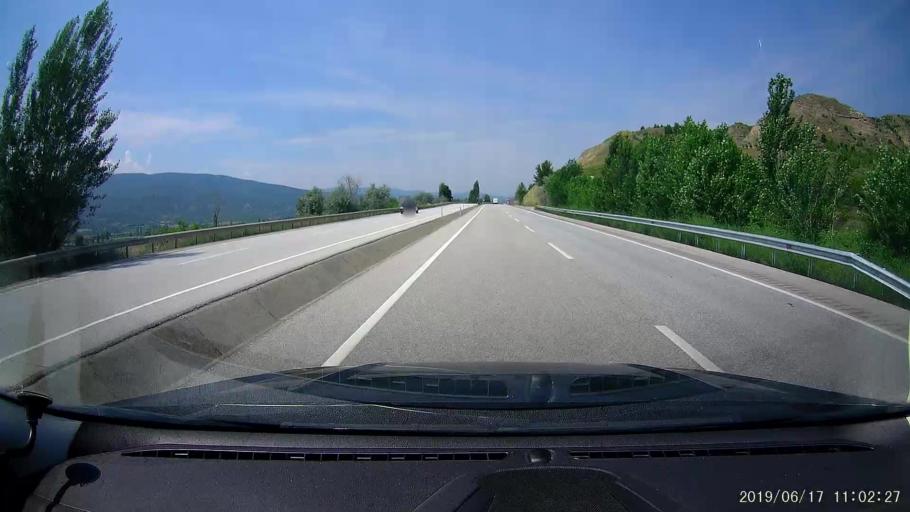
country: TR
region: Kastamonu
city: Tosya
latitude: 41.0180
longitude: 34.1362
